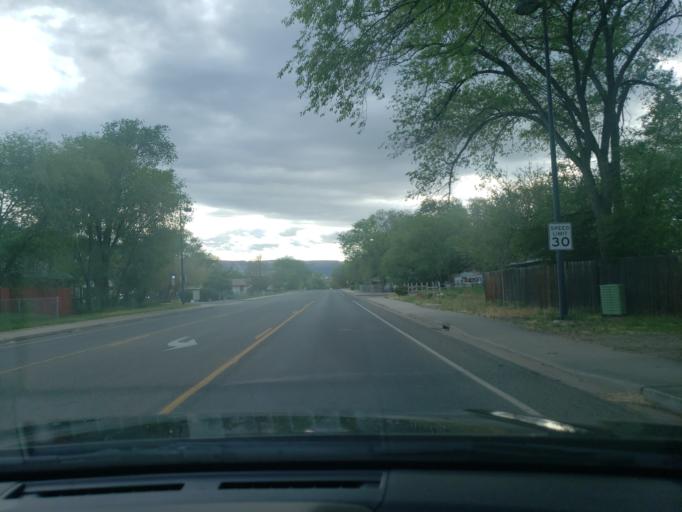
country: US
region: Colorado
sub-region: Mesa County
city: Orchard Mesa
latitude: 39.0486
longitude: -108.5592
